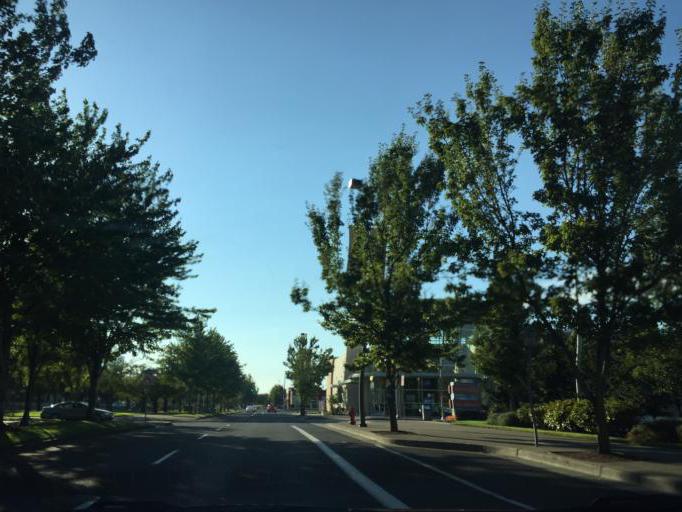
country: US
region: Washington
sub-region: Clark County
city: Orchards
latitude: 45.5741
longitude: -122.5612
